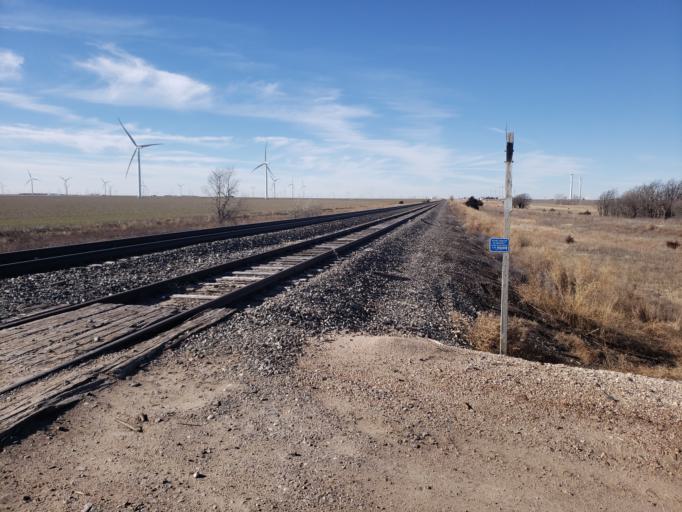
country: US
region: Kansas
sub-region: Edwards County
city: Kinsley
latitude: 37.8718
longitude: -99.6618
